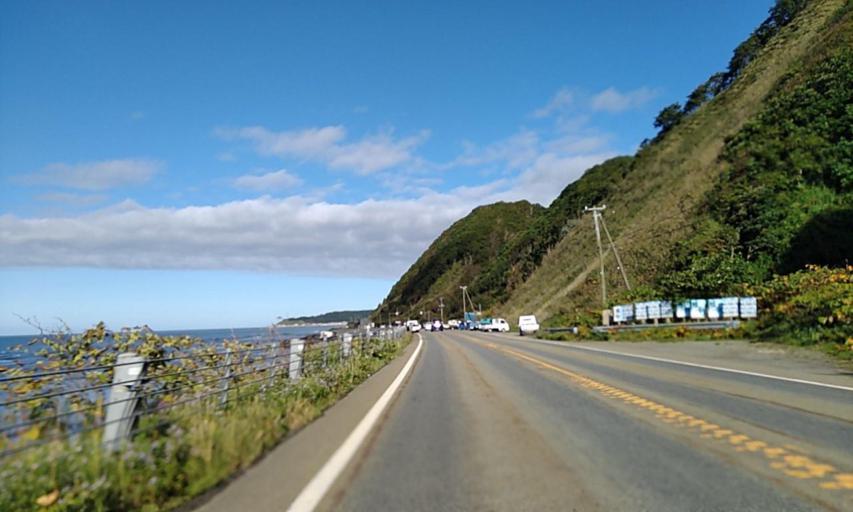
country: JP
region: Hokkaido
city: Shizunai-furukawacho
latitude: 42.2582
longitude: 142.5286
